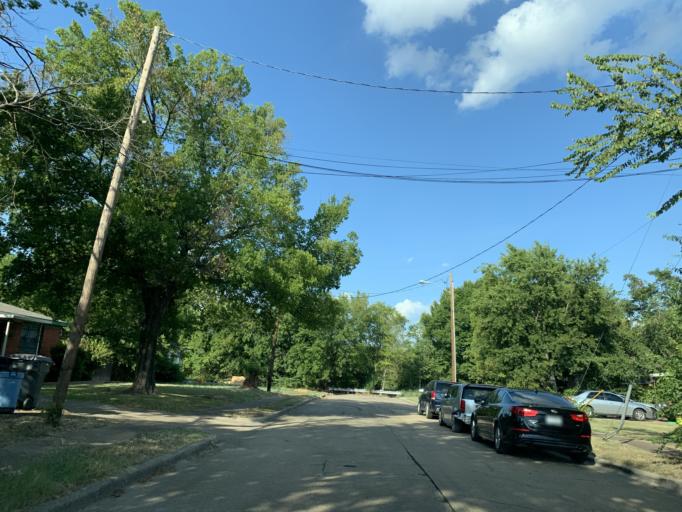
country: US
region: Texas
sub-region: Dallas County
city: Hutchins
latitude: 32.6959
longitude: -96.7787
